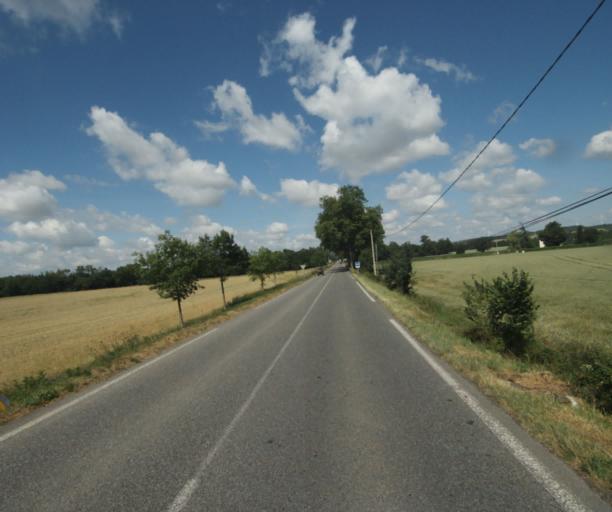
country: FR
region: Midi-Pyrenees
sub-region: Departement de la Haute-Garonne
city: Revel
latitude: 43.4455
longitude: 1.9513
